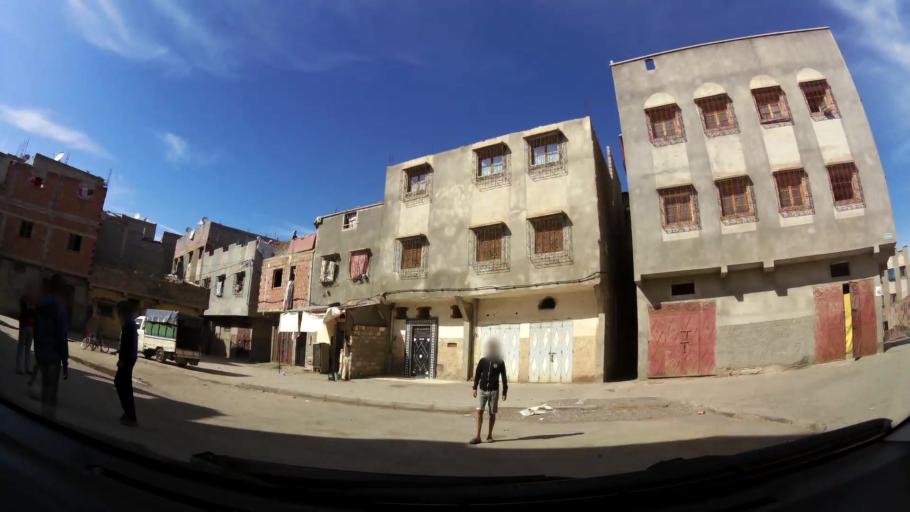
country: MA
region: Marrakech-Tensift-Al Haouz
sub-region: Marrakech
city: Marrakesh
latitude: 31.6371
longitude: -7.9762
